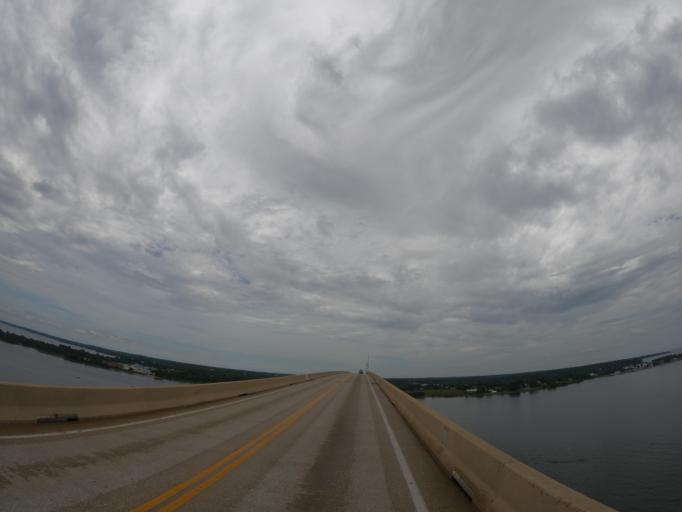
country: US
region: Maryland
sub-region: Calvert County
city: Solomons
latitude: 38.3239
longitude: -76.4742
